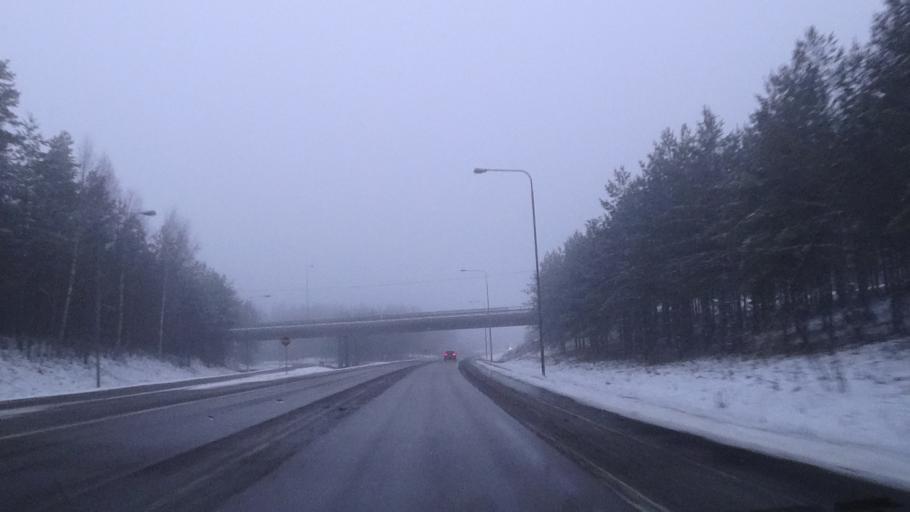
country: FI
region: Paijanne Tavastia
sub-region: Lahti
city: Hollola
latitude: 60.9831
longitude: 25.4229
